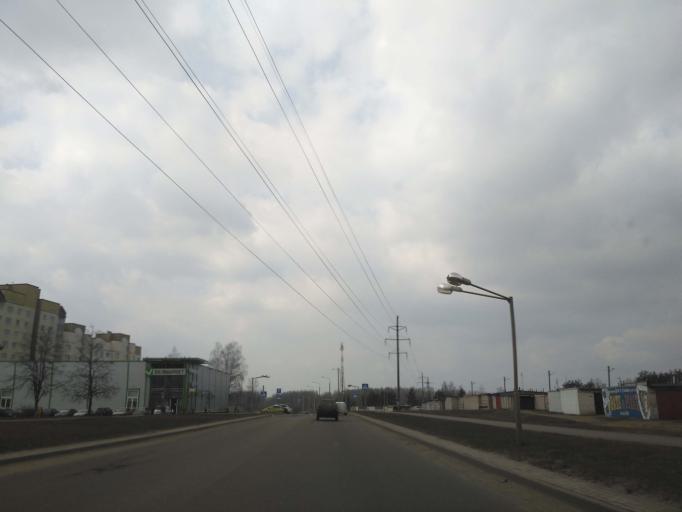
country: BY
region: Minsk
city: Horad Barysaw
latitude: 54.2163
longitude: 28.4741
